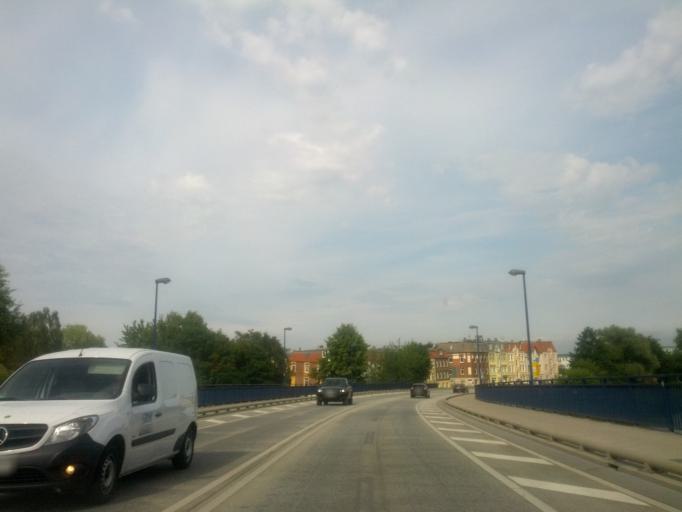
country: DE
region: Mecklenburg-Vorpommern
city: Wismar
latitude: 53.8929
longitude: 11.4751
